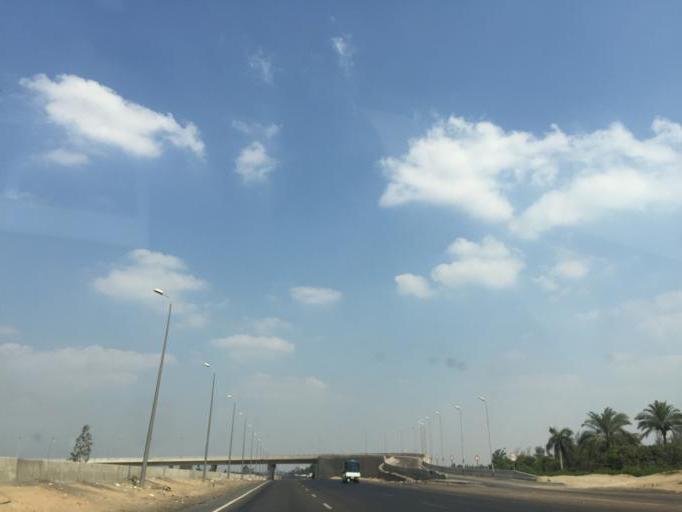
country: EG
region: Al Buhayrah
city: Beheira
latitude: 30.3170
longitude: 30.5417
